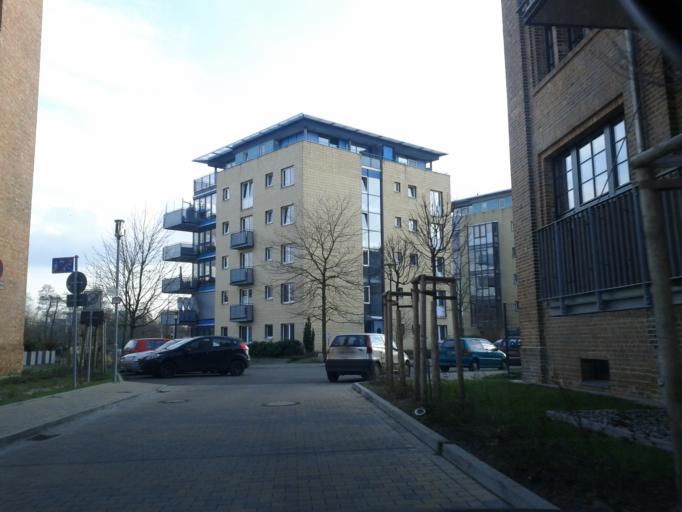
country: DE
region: Berlin
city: Berlin Koepenick
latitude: 52.4490
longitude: 13.5851
